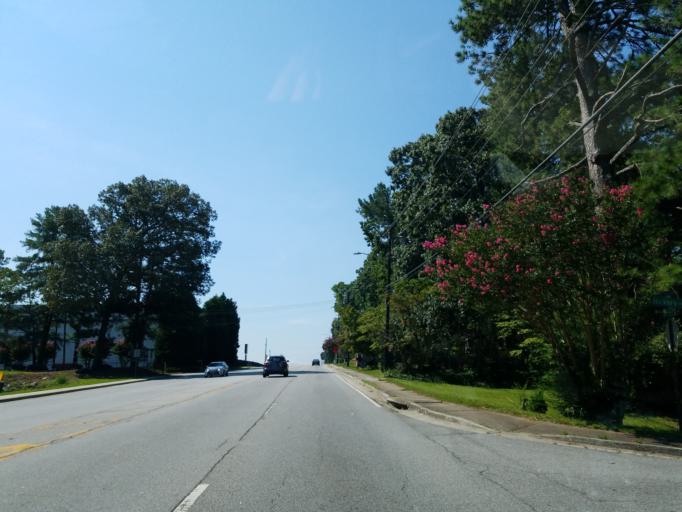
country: US
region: Georgia
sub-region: DeKalb County
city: Chamblee
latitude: 33.8797
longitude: -84.3095
